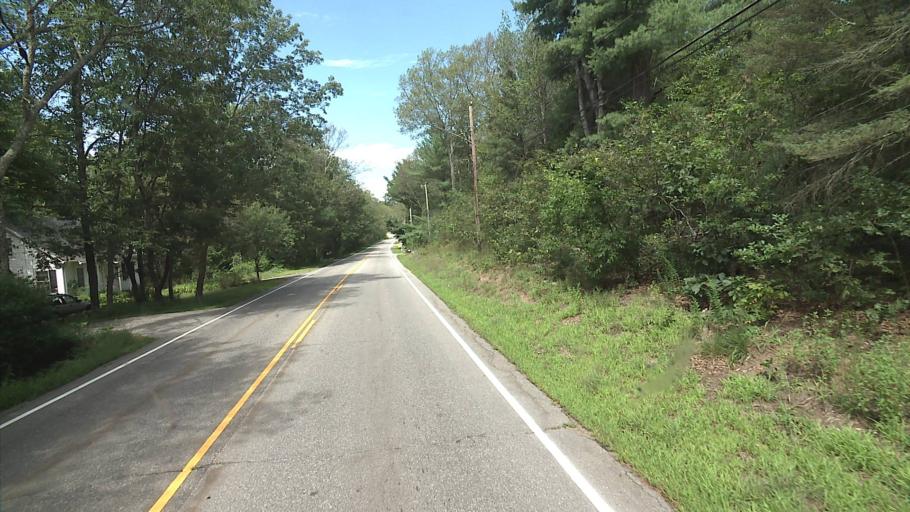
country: US
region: Connecticut
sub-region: Tolland County
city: Mansfield City
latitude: 41.7768
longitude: -72.2098
